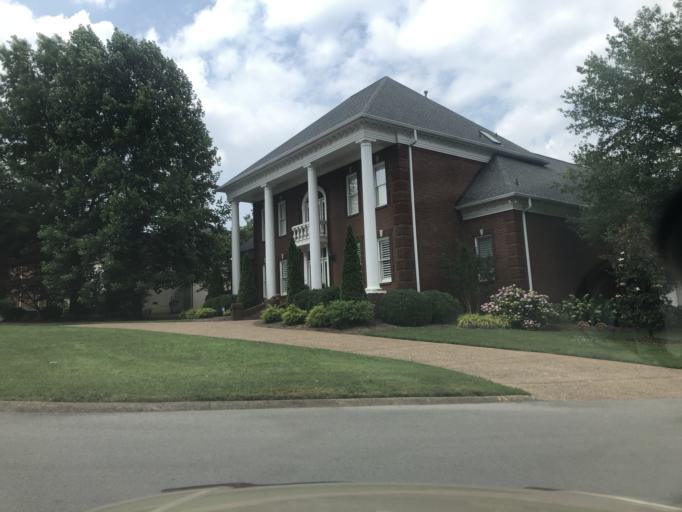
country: US
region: Tennessee
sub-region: Davidson County
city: Lakewood
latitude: 36.2384
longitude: -86.6059
